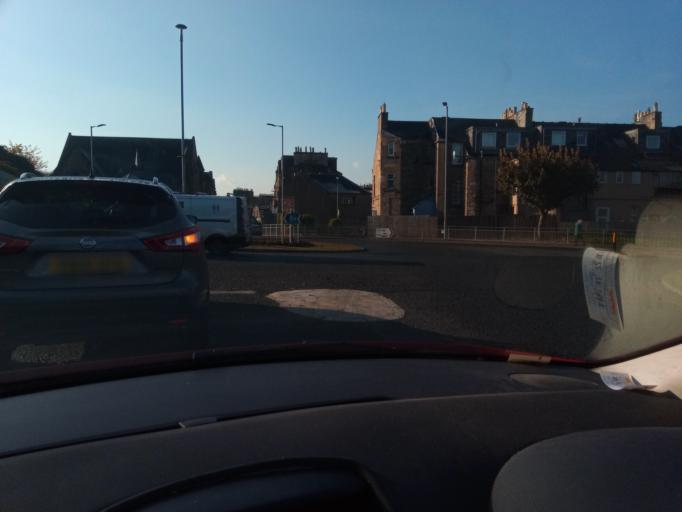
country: GB
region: Scotland
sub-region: The Scottish Borders
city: Hawick
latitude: 55.4262
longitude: -2.7825
